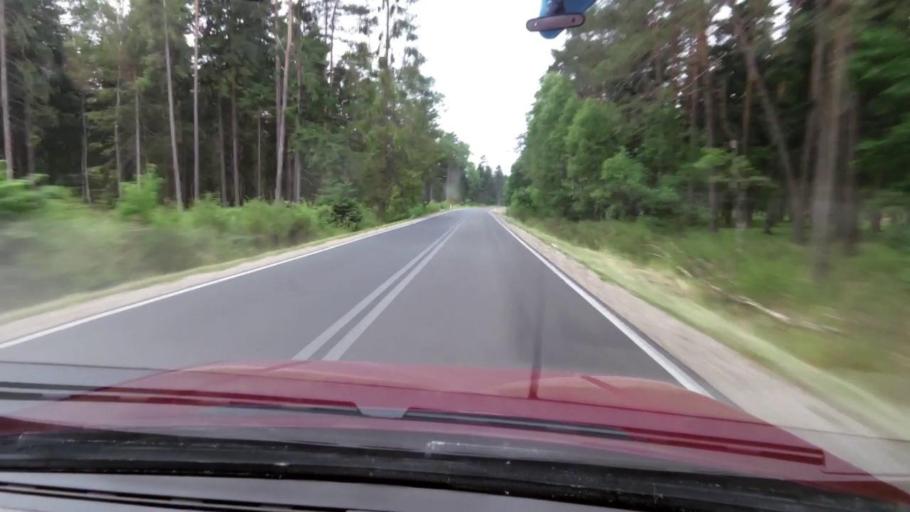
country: PL
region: West Pomeranian Voivodeship
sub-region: Powiat koszalinski
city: Sianow
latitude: 54.1504
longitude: 16.4707
